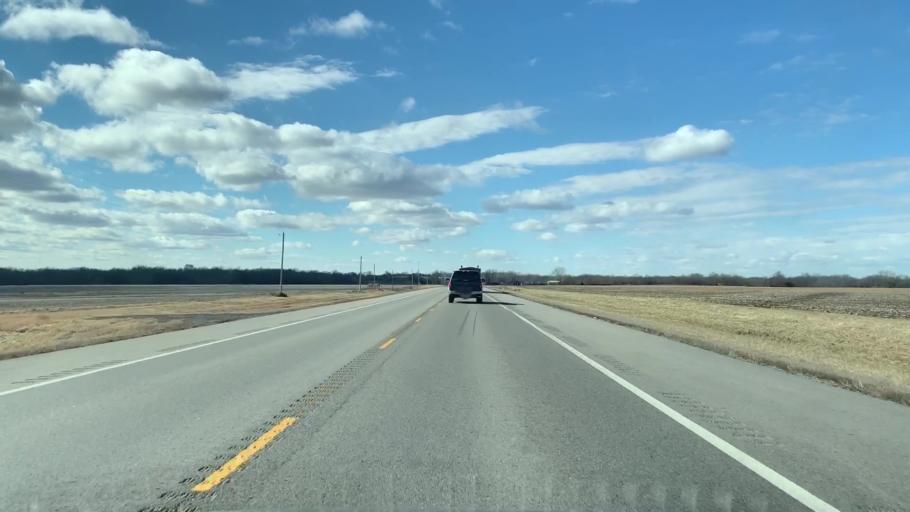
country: US
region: Kansas
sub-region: Cherokee County
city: Columbus
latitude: 37.3398
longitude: -94.8730
